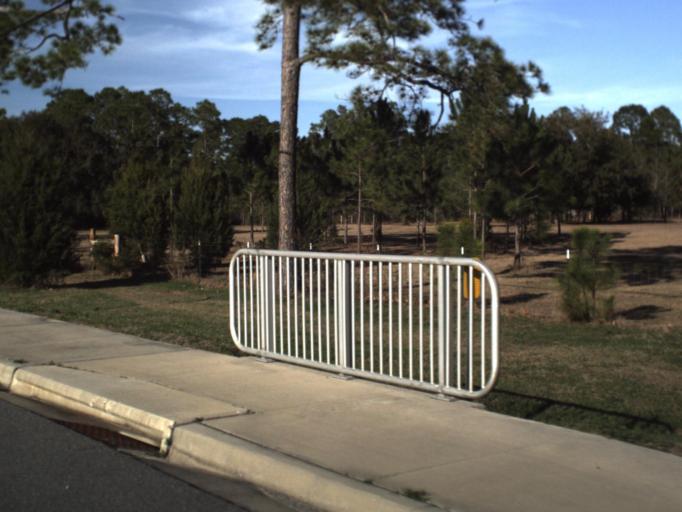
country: US
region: Florida
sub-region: Bay County
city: Laguna Beach
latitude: 30.3267
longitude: -85.8570
